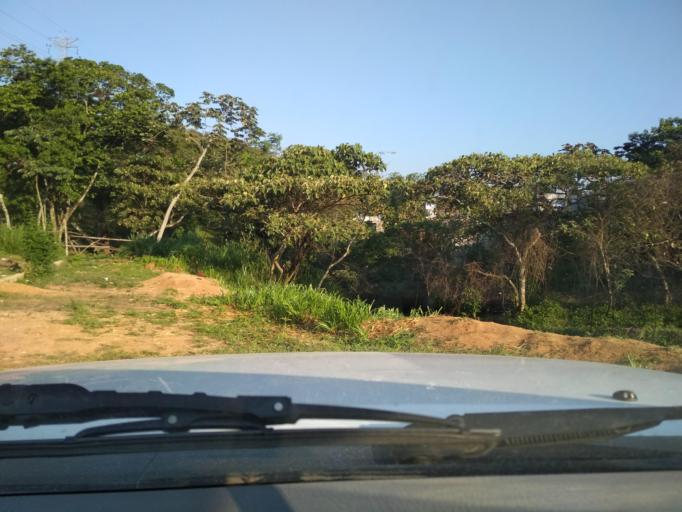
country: MX
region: Veracruz
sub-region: Cordoba
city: Veinte de Noviembre
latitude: 18.8700
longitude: -96.9397
